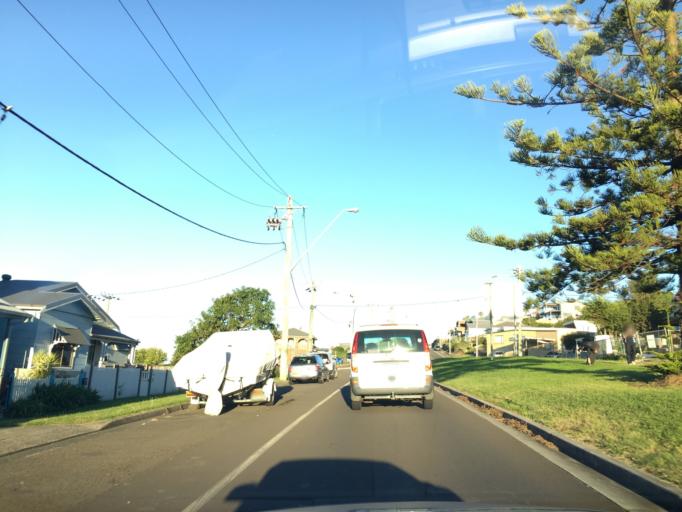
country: AU
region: New South Wales
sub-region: Kiama
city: Kiama
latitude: -34.6628
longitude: 150.8510
